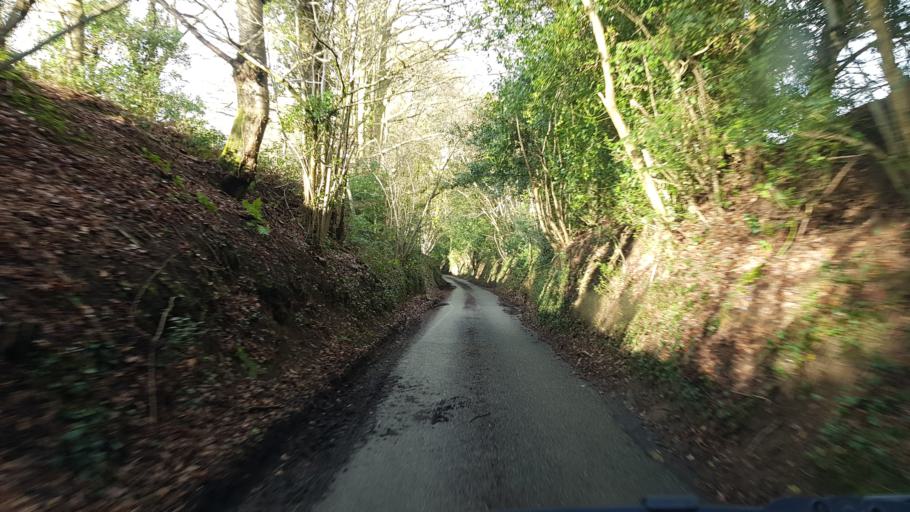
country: GB
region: England
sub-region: Surrey
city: Churt
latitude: 51.1322
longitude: -0.7820
